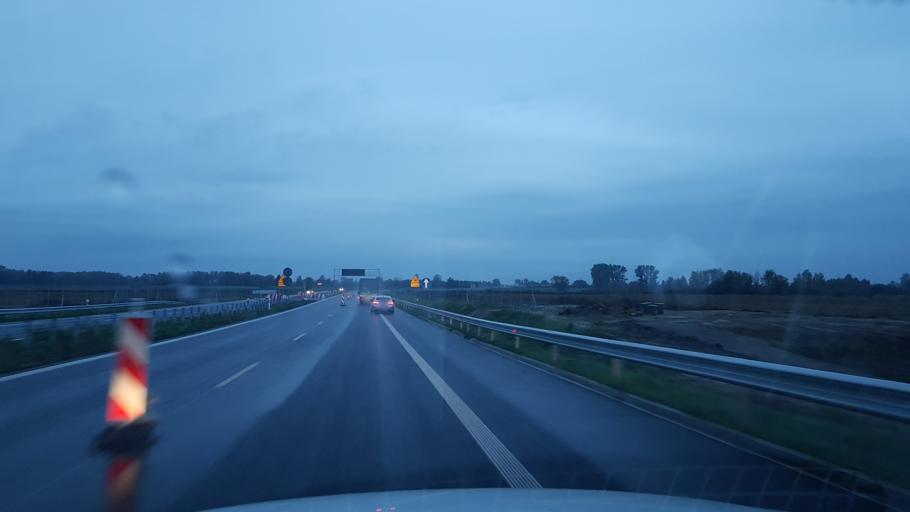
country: PL
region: West Pomeranian Voivodeship
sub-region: Powiat gryficki
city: Ploty
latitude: 53.8023
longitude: 15.2514
